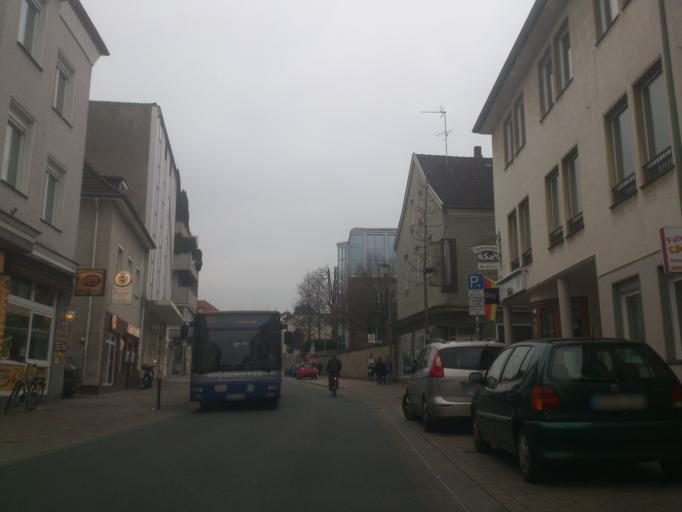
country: DE
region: North Rhine-Westphalia
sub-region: Regierungsbezirk Detmold
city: Paderborn
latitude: 51.7211
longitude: 8.7570
